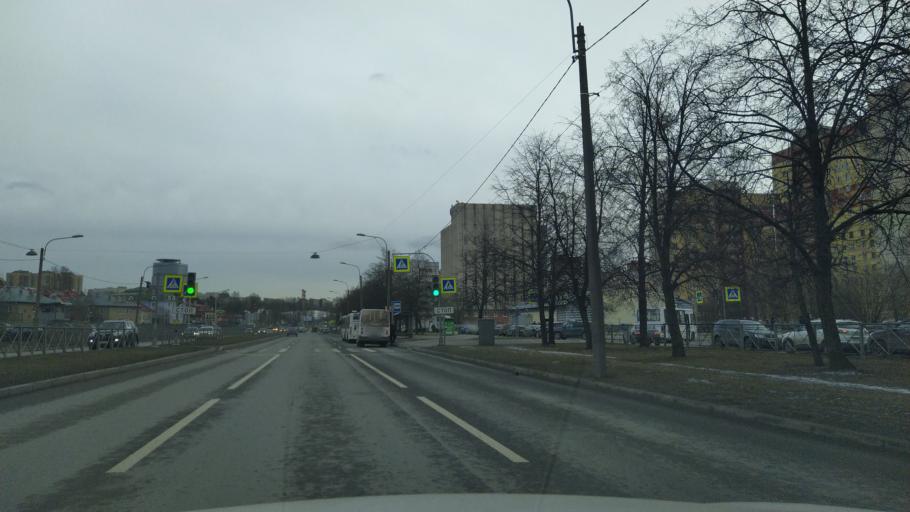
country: RU
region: St.-Petersburg
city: Kolomyagi
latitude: 60.0162
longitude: 30.2861
